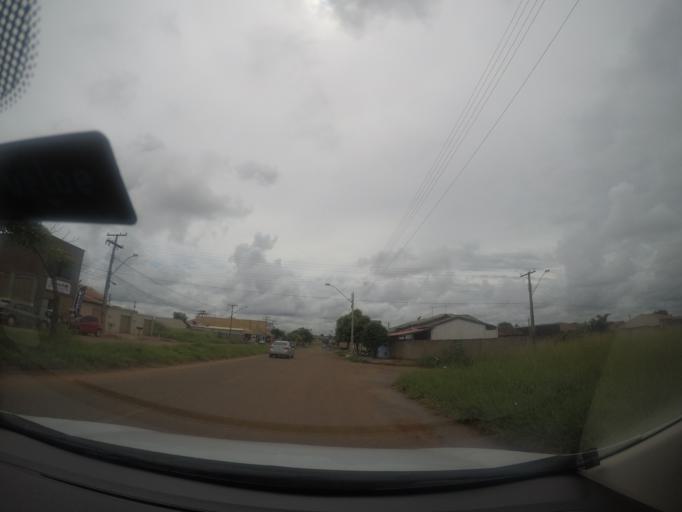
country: BR
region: Goias
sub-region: Trindade
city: Trindade
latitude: -16.6923
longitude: -49.4002
